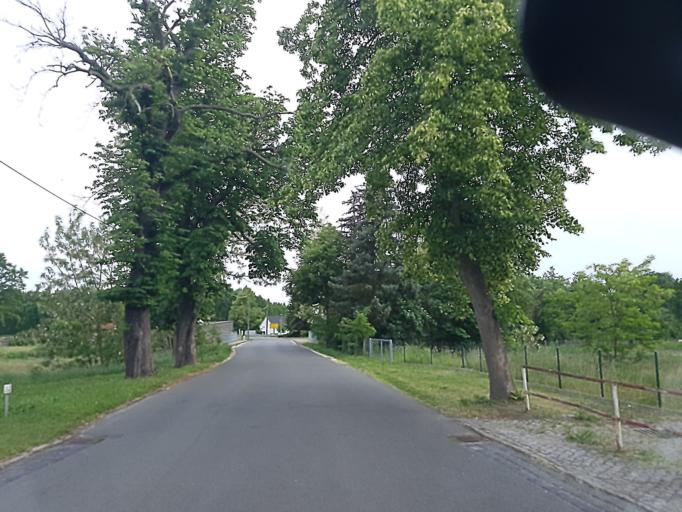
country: DE
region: Saxony-Anhalt
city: Holzdorf
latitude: 51.7788
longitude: 13.1139
